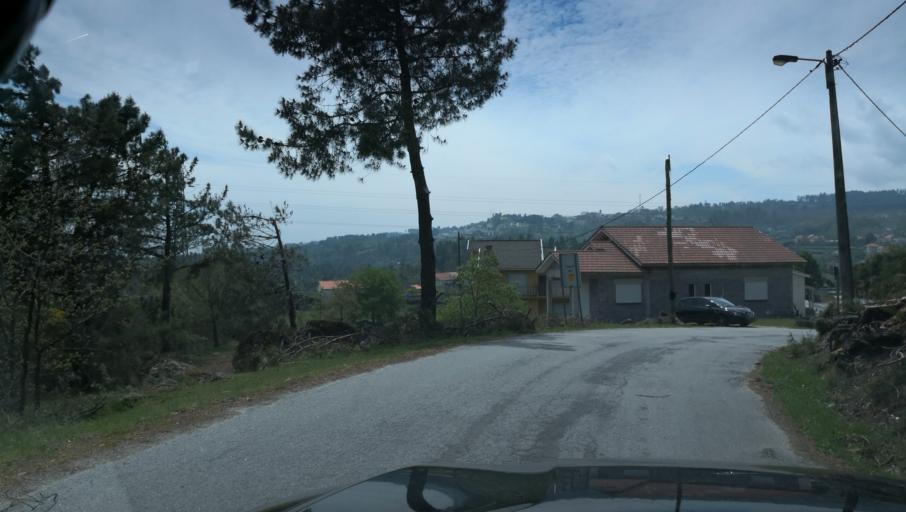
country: PT
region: Vila Real
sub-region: Vila Real
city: Vila Real
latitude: 41.2869
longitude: -7.8071
